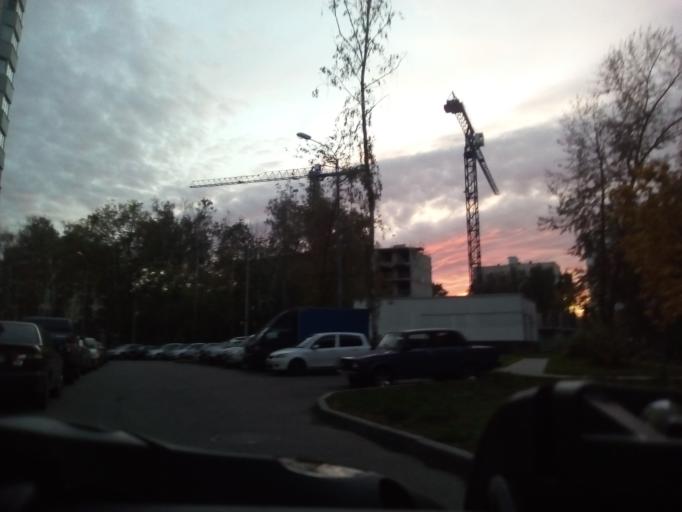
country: RU
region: Moscow
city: Sviblovo
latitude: 55.8566
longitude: 37.6410
